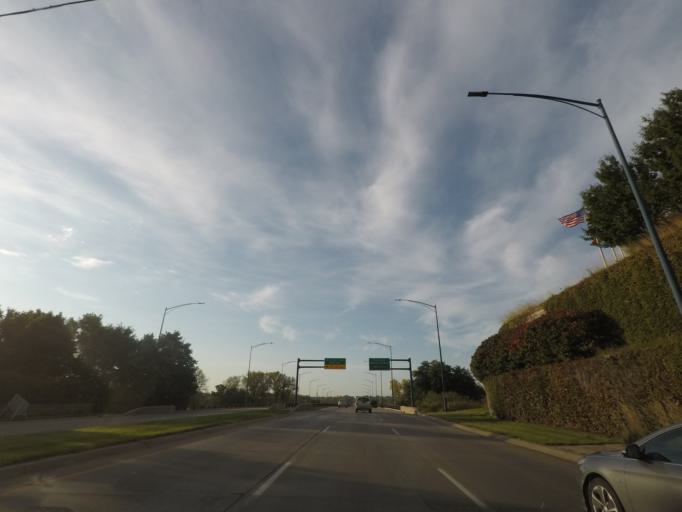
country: US
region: Iowa
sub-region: Polk County
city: Des Moines
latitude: 41.5838
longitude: -93.6449
